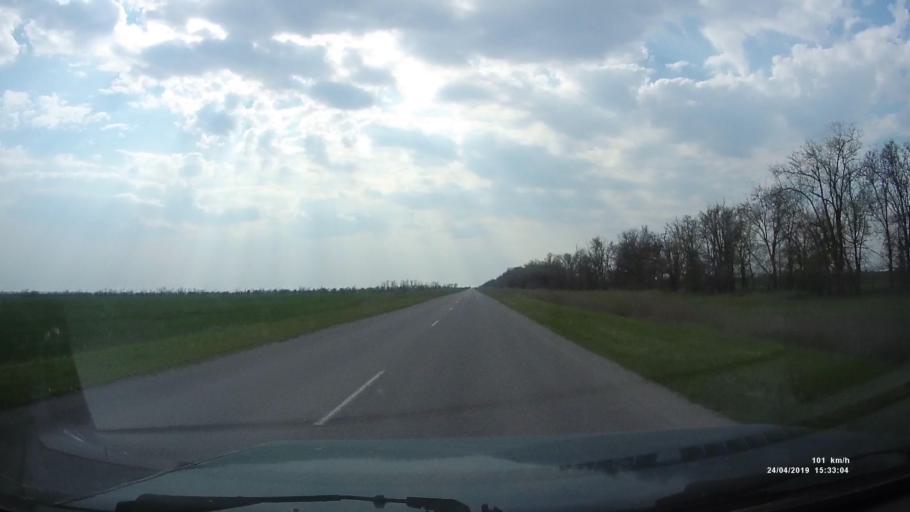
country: RU
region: Rostov
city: Remontnoye
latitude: 46.5997
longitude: 42.9464
